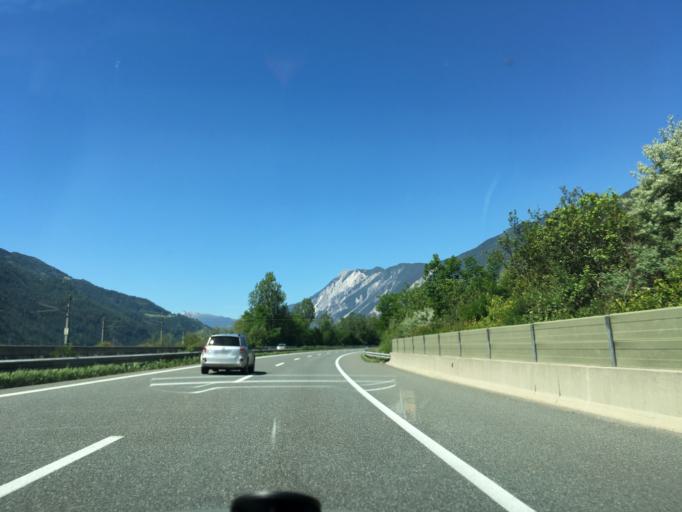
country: AT
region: Tyrol
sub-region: Politischer Bezirk Imst
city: Motz
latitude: 47.2729
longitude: 10.9539
